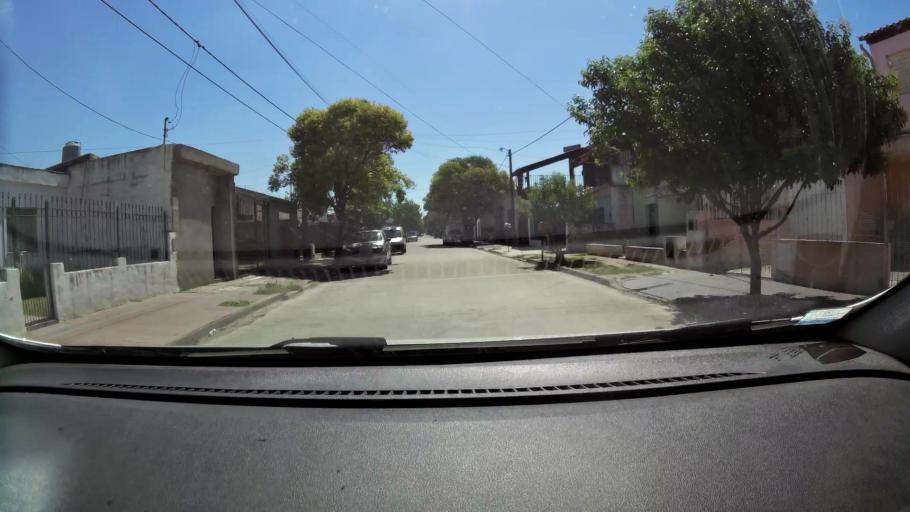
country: AR
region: Cordoba
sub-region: Departamento de Capital
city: Cordoba
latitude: -31.3707
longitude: -64.1335
